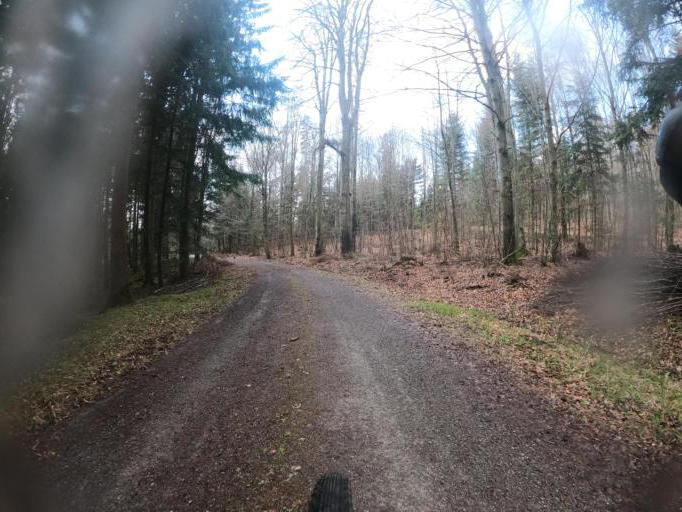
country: DE
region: Baden-Wuerttemberg
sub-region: Karlsruhe Region
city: Neuweiler
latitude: 48.7067
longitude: 8.5765
